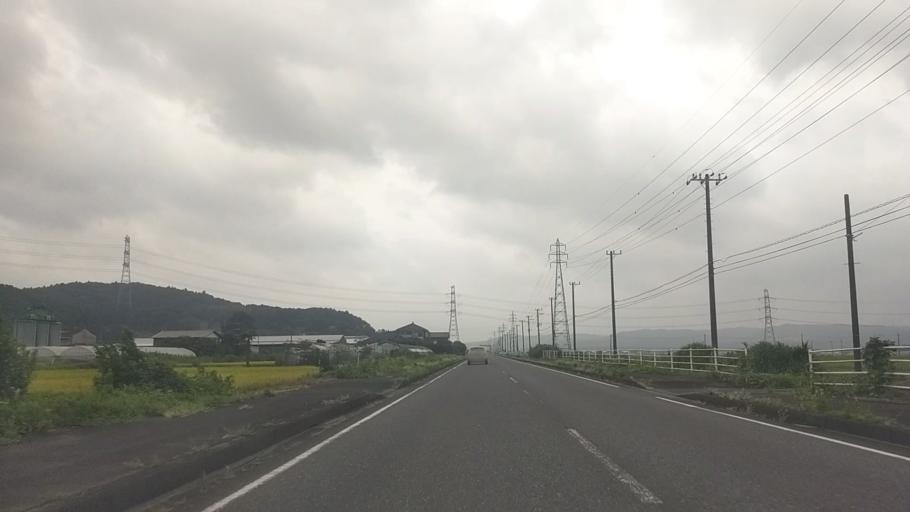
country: JP
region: Chiba
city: Kisarazu
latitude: 35.3496
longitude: 140.0548
